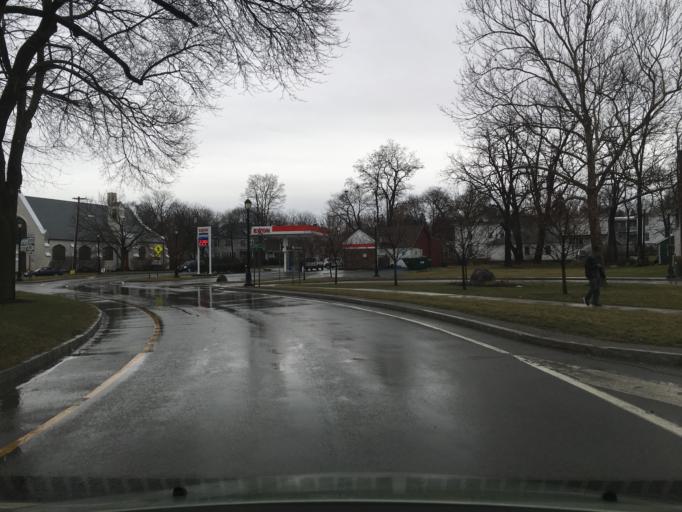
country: US
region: New York
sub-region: Livingston County
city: Avon
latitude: 42.9114
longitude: -77.7455
